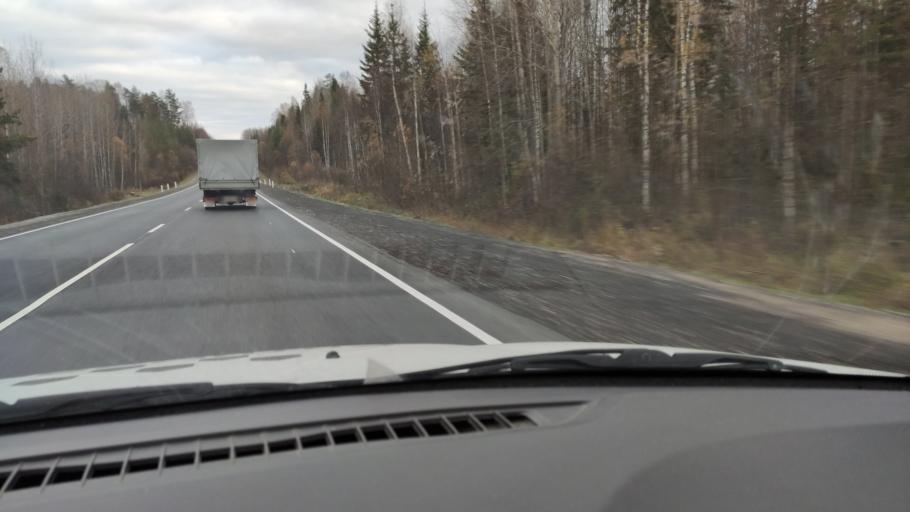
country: RU
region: Kirov
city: Chernaya Kholunitsa
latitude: 58.8724
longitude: 51.5222
